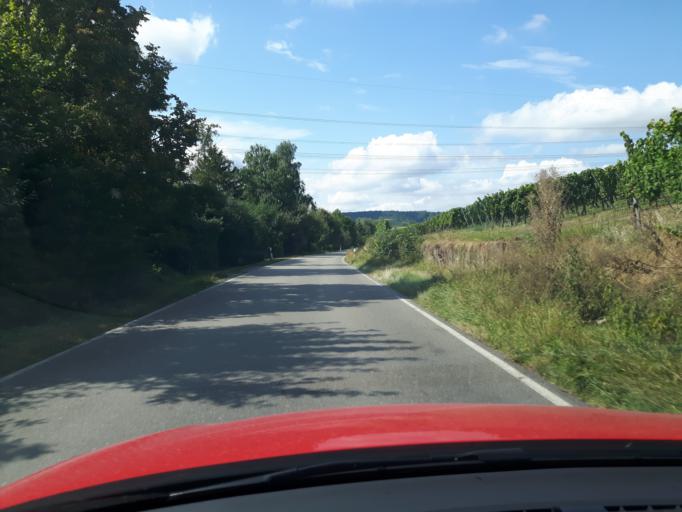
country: DE
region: Baden-Wuerttemberg
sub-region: Regierungsbezirk Stuttgart
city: Nordheim
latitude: 49.1112
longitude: 9.1199
